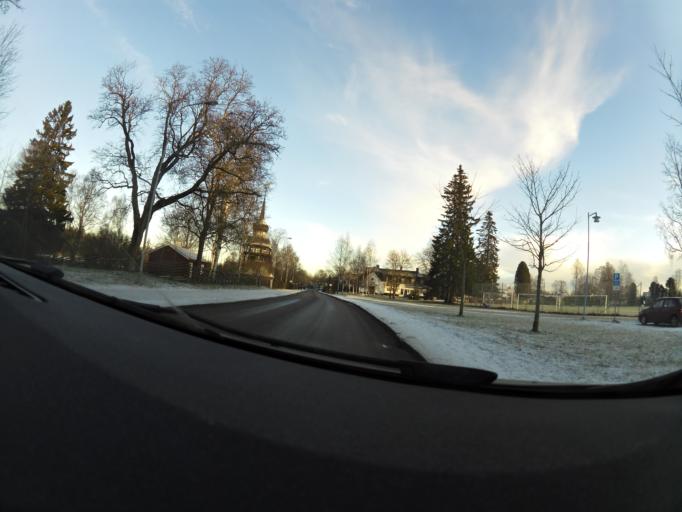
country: SE
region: Gaevleborg
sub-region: Gavle Kommun
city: Gavle
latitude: 60.6699
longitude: 17.1205
